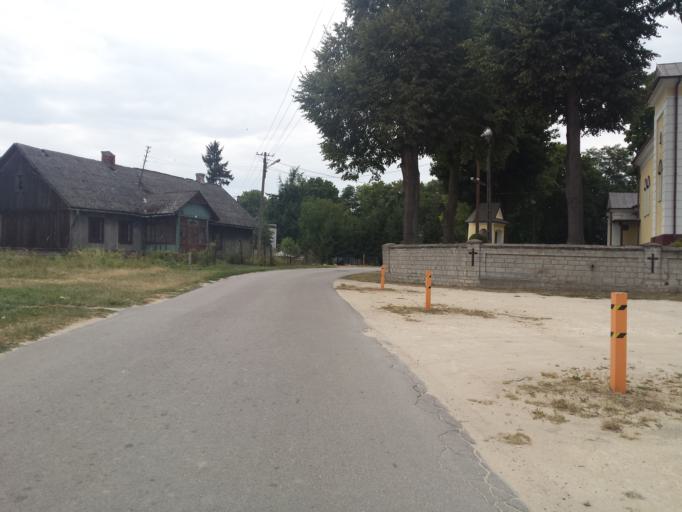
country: PL
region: Swietokrzyskie
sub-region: Powiat staszowski
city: Bogoria
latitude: 50.6664
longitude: 21.2444
